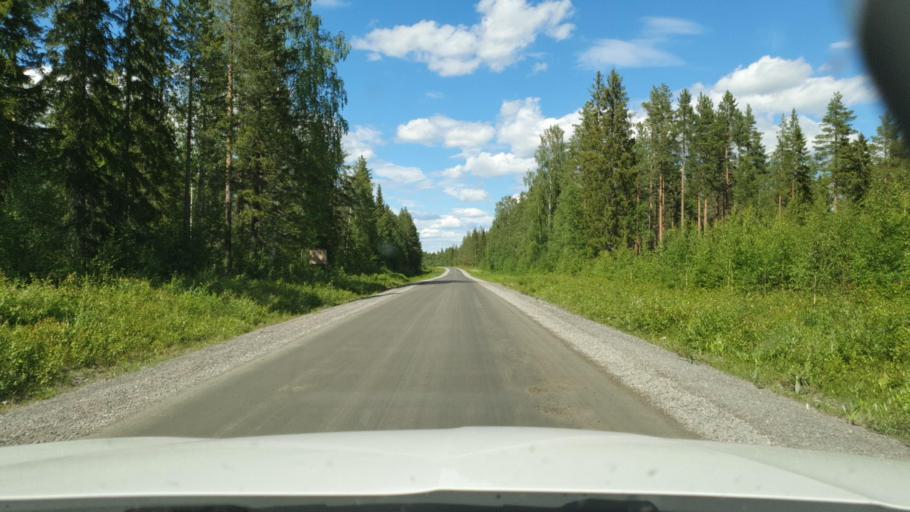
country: SE
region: Vaesterbotten
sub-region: Skelleftea Kommun
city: Forsbacka
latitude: 64.8009
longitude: 20.5036
